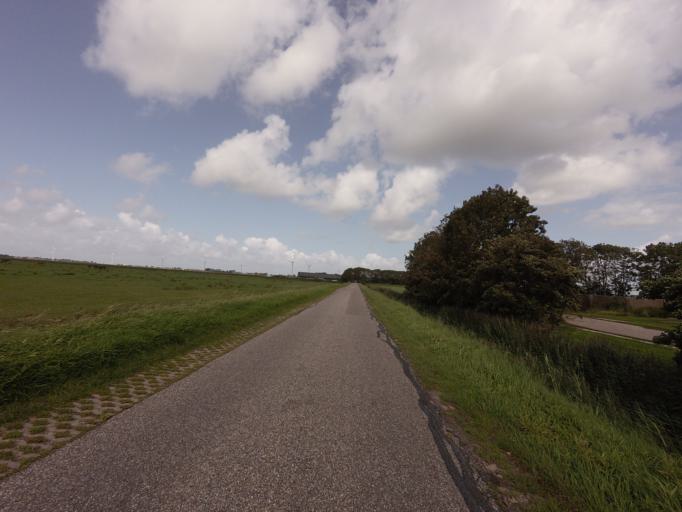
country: NL
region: Friesland
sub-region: Gemeente Franekeradeel
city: Sexbierum
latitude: 53.1702
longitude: 5.4886
